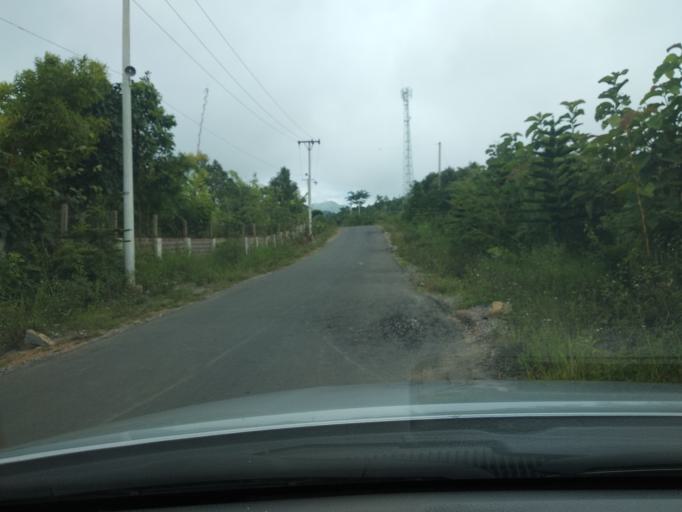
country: MM
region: Mandalay
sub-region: Pyin Oo Lwin District
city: Pyin Oo Lwin
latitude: 21.9218
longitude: 96.3771
